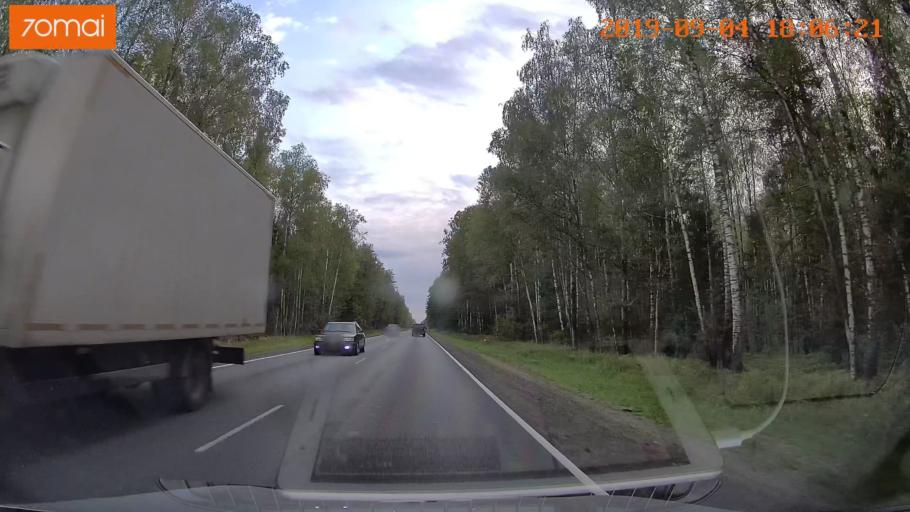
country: RU
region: Moskovskaya
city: Khorlovo
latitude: 55.4321
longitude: 38.8159
